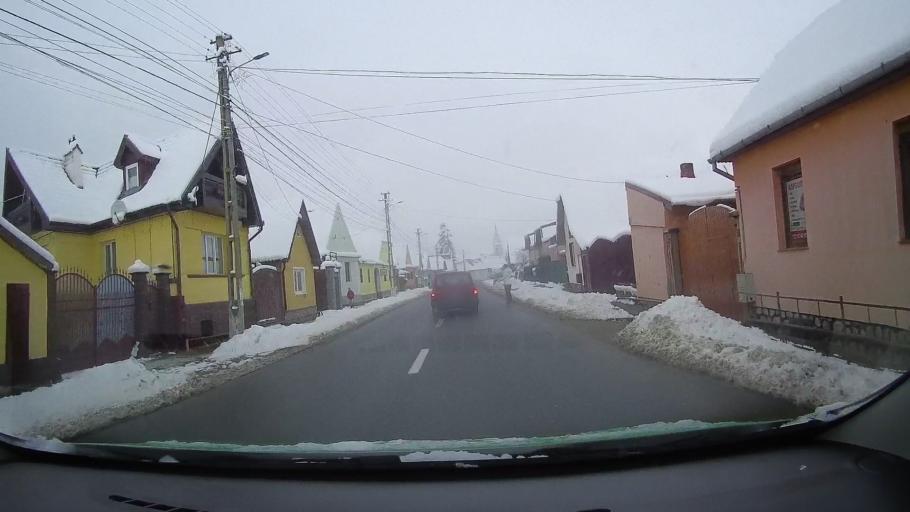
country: RO
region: Sibiu
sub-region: Comuna Cristian
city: Cristian
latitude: 45.7789
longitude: 24.0278
